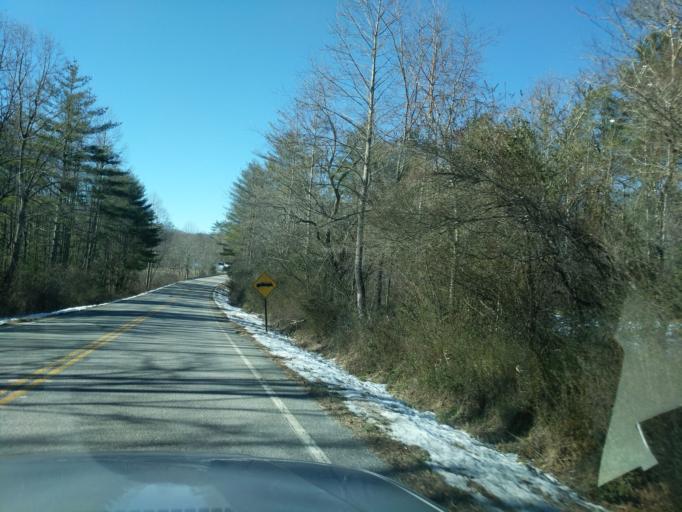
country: US
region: Georgia
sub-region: Towns County
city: Hiawassee
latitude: 34.9267
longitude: -83.6393
